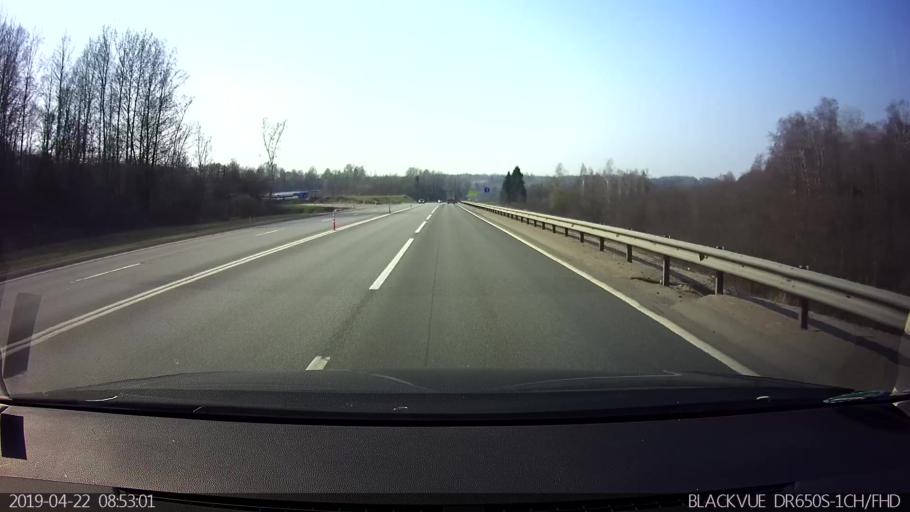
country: RU
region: Smolensk
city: Pechersk
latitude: 54.9002
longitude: 32.1196
